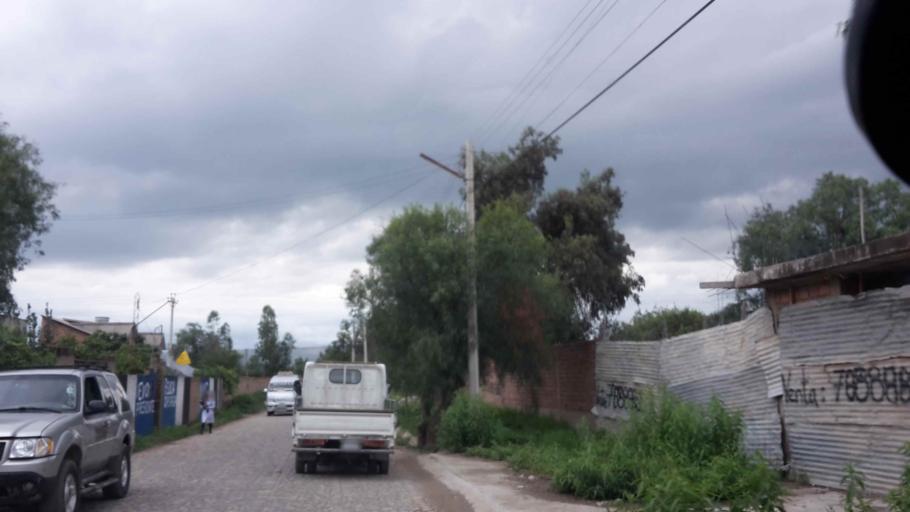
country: BO
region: Cochabamba
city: Cochabamba
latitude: -17.3663
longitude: -66.2140
